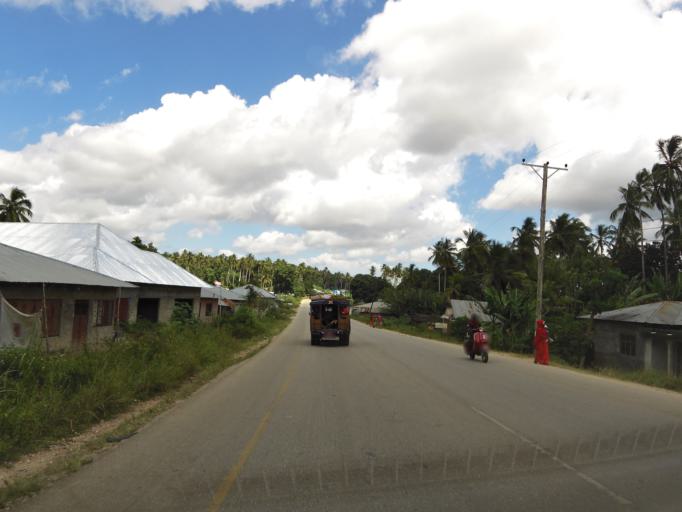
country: TZ
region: Zanzibar Central/South
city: Koani
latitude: -6.1381
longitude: 39.2859
